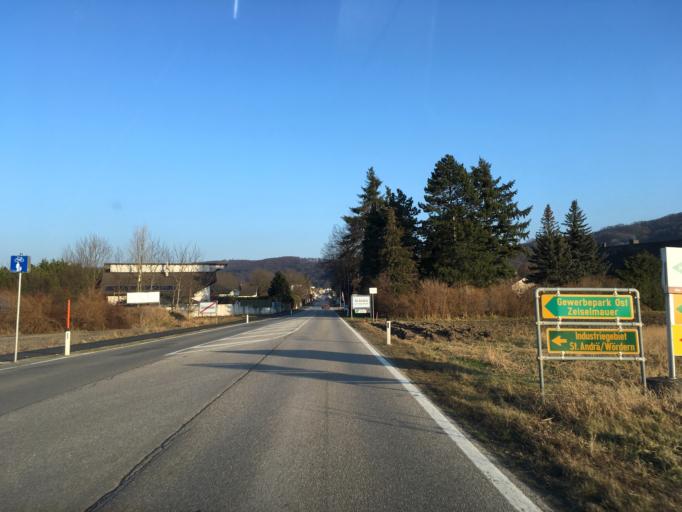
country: AT
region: Lower Austria
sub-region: Politischer Bezirk Tulln
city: Wordern
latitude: 48.3235
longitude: 16.1917
